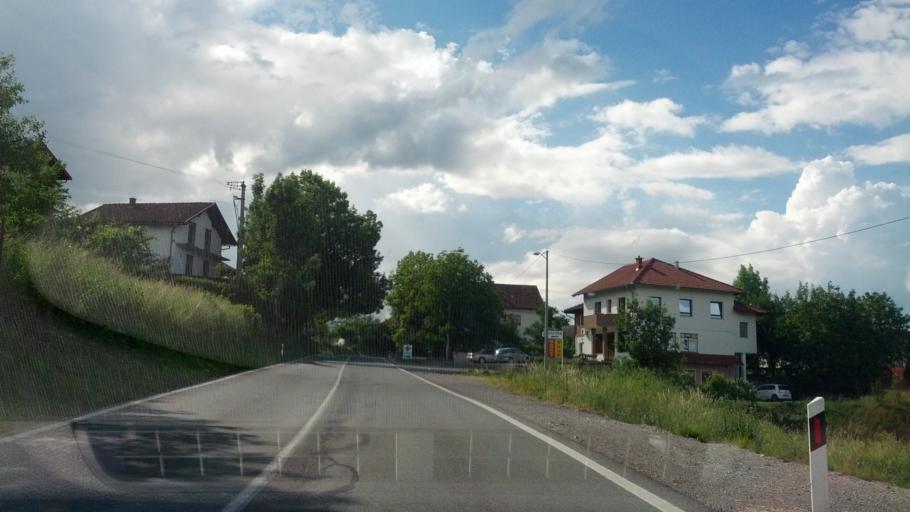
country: BA
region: Federation of Bosnia and Herzegovina
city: Izacic
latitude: 44.8726
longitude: 15.7838
